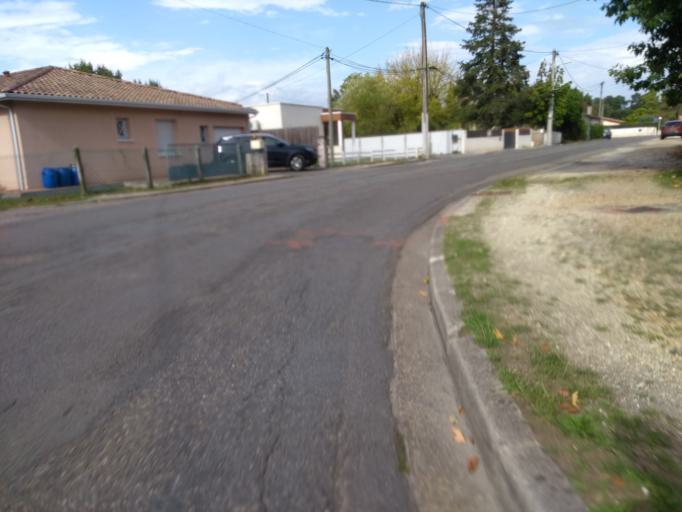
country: FR
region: Aquitaine
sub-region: Departement de la Gironde
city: Gradignan
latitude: 44.7809
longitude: -0.6235
